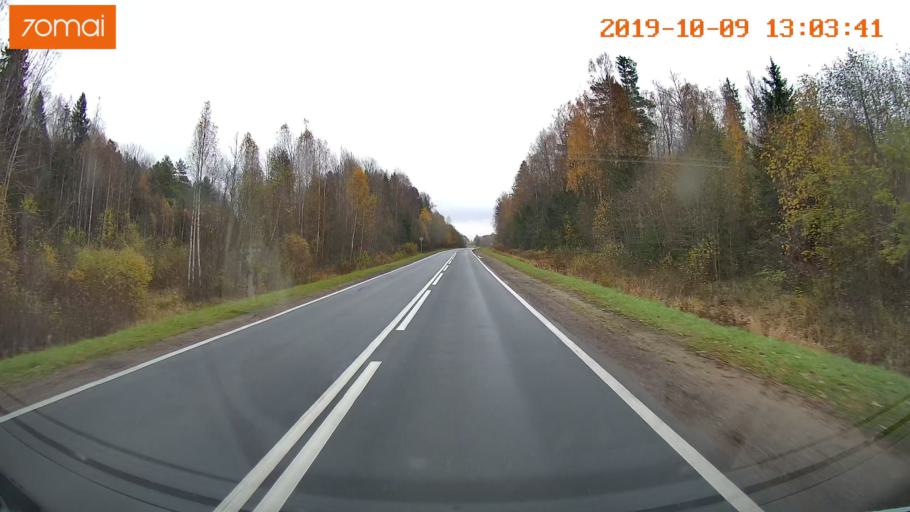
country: RU
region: Jaroslavl
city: Lyubim
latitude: 58.3591
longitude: 40.5334
